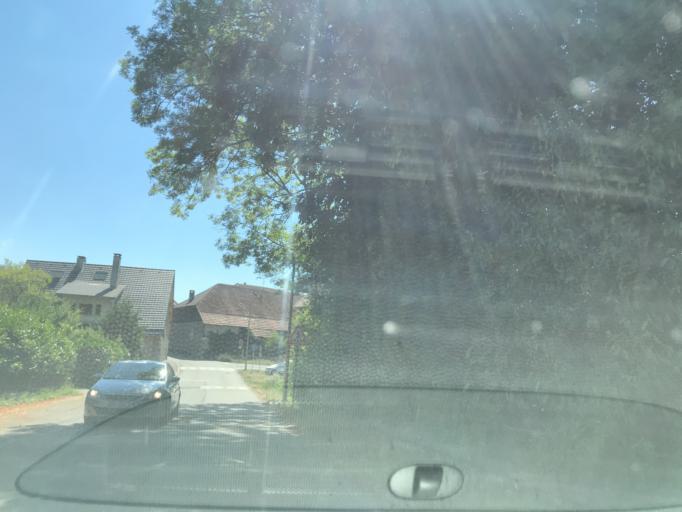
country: FR
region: Rhone-Alpes
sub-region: Departement de la Haute-Savoie
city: Villaz
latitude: 45.9355
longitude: 6.1914
